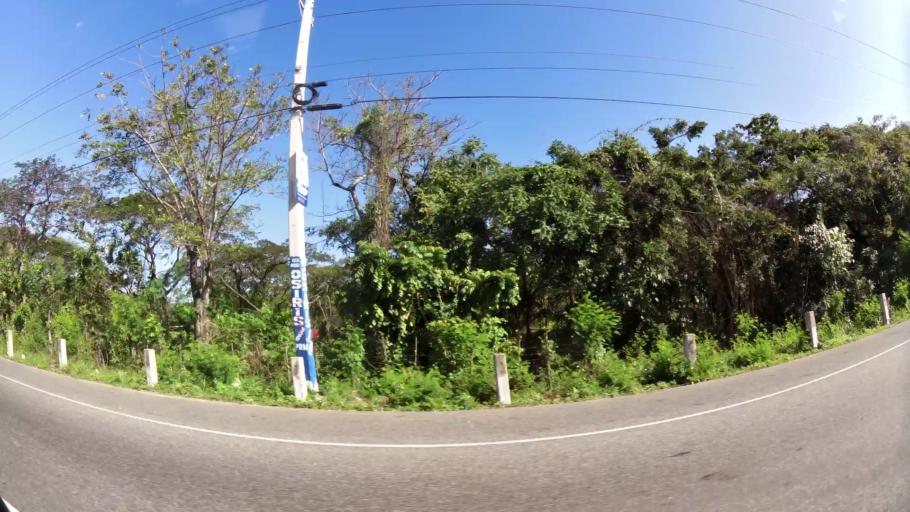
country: DO
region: San Cristobal
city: San Cristobal
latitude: 18.4317
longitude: -70.1072
